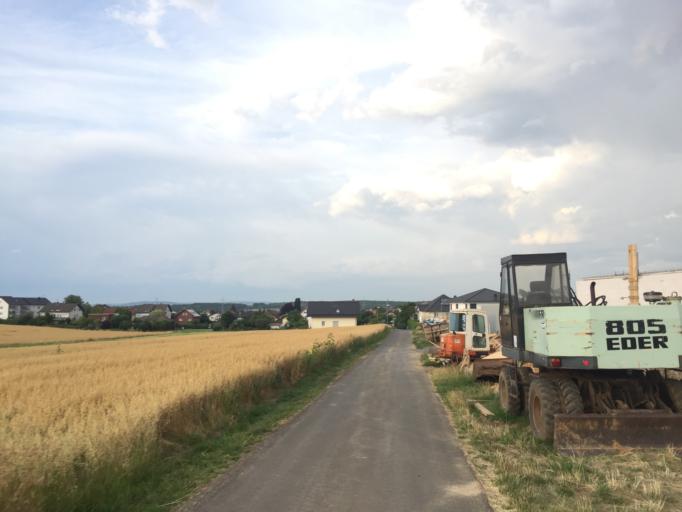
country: DE
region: Hesse
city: Allendorf an der Lahn
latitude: 50.5338
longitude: 8.6136
